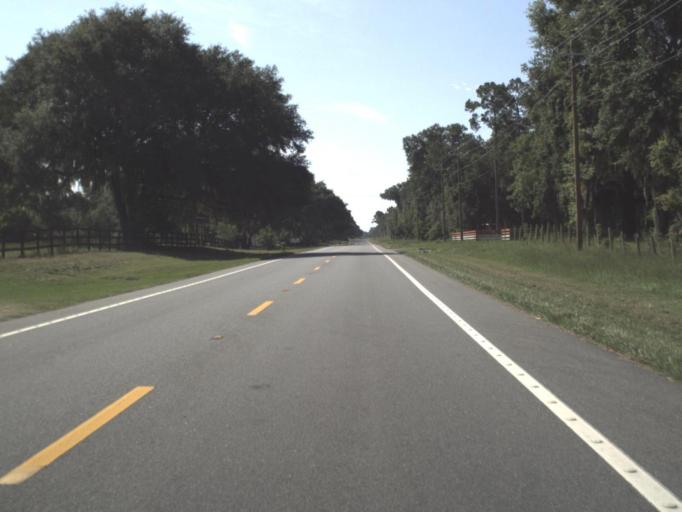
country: US
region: Florida
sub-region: Madison County
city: Madison
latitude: 30.4287
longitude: -83.3857
